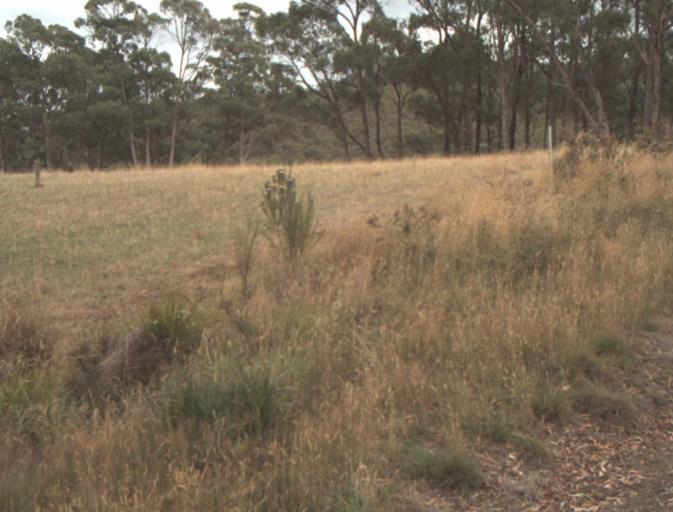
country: AU
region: Tasmania
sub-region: Dorset
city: Scottsdale
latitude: -41.4665
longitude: 147.5740
